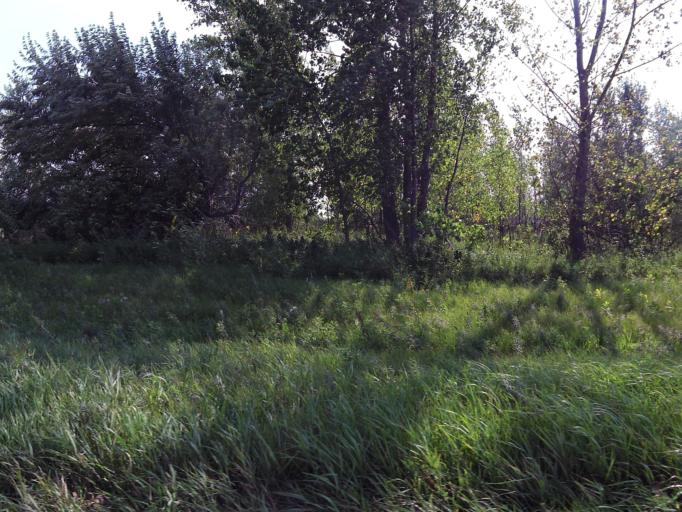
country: US
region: North Dakota
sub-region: Walsh County
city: Grafton
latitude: 48.4308
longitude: -97.4004
